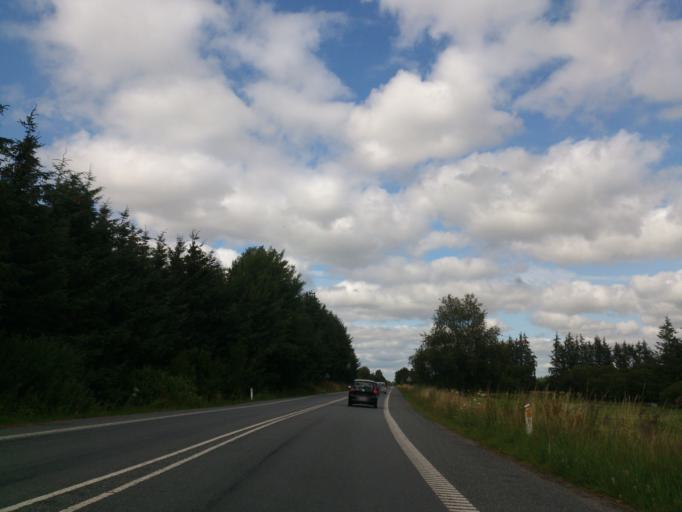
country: DK
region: South Denmark
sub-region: Aabenraa Kommune
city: Krusa
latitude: 54.8686
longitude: 9.4053
